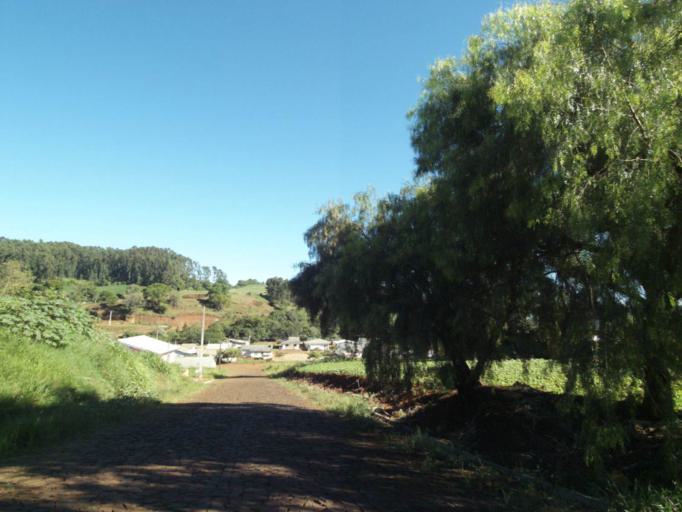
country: BR
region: Santa Catarina
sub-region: Sao Lourenco Do Oeste
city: Sao Lourenco dOeste
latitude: -26.2671
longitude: -52.7856
